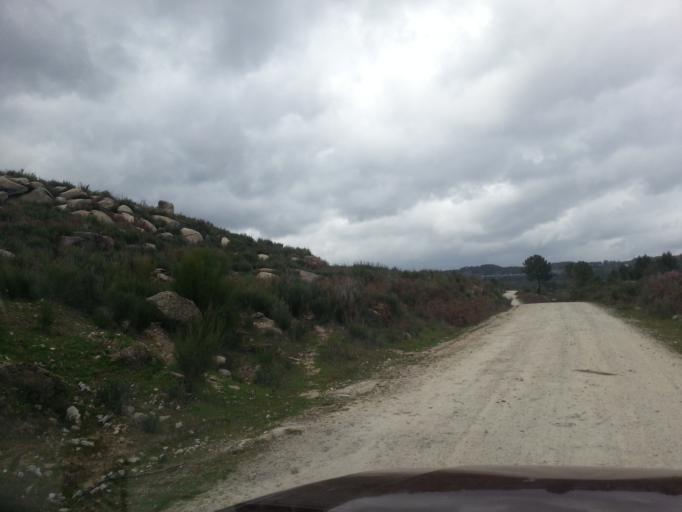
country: PT
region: Guarda
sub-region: Fornos de Algodres
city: Fornos de Algodres
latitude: 40.5900
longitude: -7.5671
